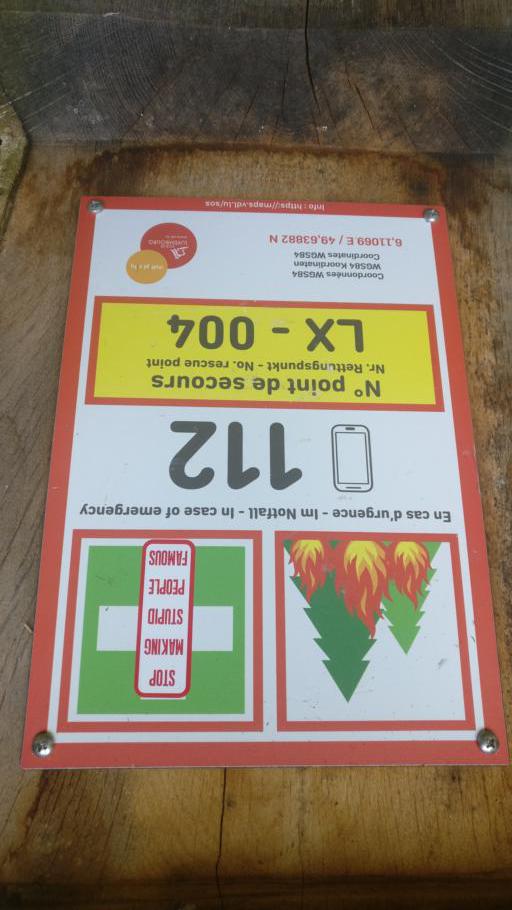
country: LU
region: Luxembourg
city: Bereldange
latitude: 49.6387
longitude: 6.1105
